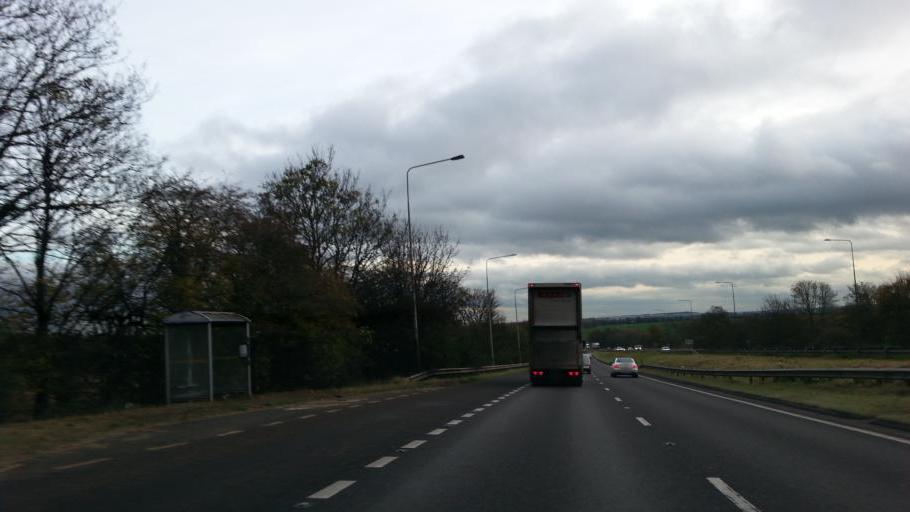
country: GB
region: England
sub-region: Doncaster
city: Campsall
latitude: 53.6076
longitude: -1.2220
